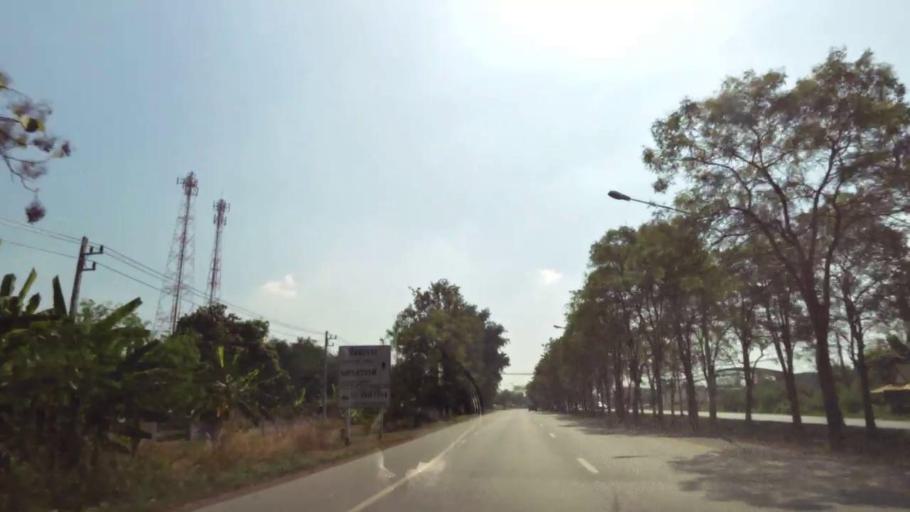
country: TH
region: Phichit
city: Bueng Na Rang
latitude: 16.1918
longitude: 100.1286
